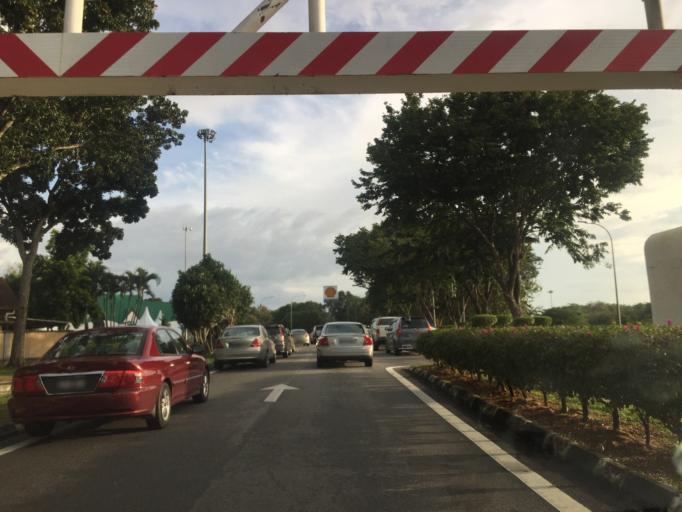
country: MY
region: Kedah
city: Gurun
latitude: 5.8319
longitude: 100.4885
